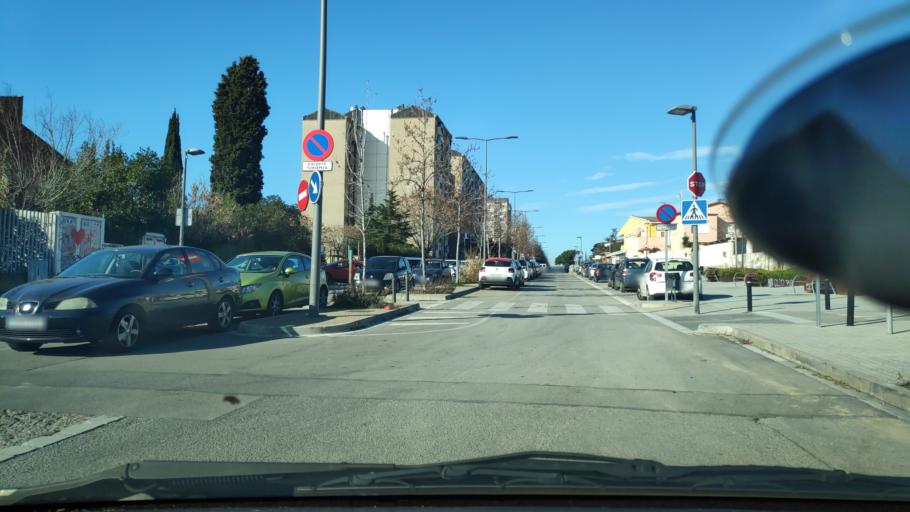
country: ES
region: Catalonia
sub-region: Provincia de Barcelona
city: Barbera del Valles
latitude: 41.5057
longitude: 2.1229
